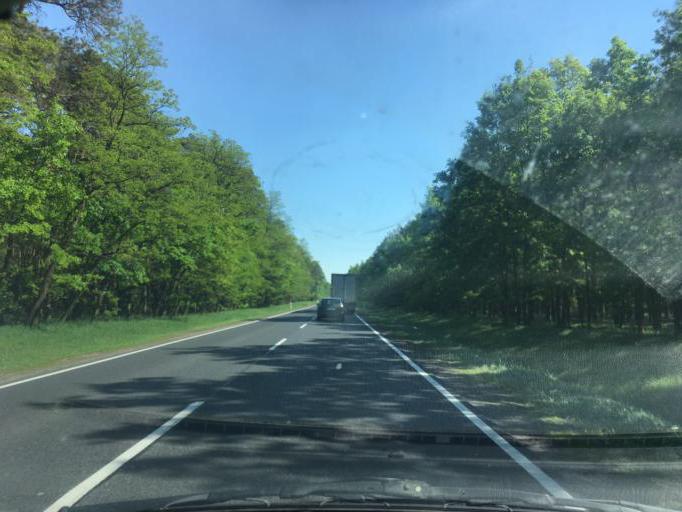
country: PL
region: Kujawsko-Pomorskie
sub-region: Powiat torunski
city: Wielka Nieszawka
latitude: 53.0261
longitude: 18.4184
